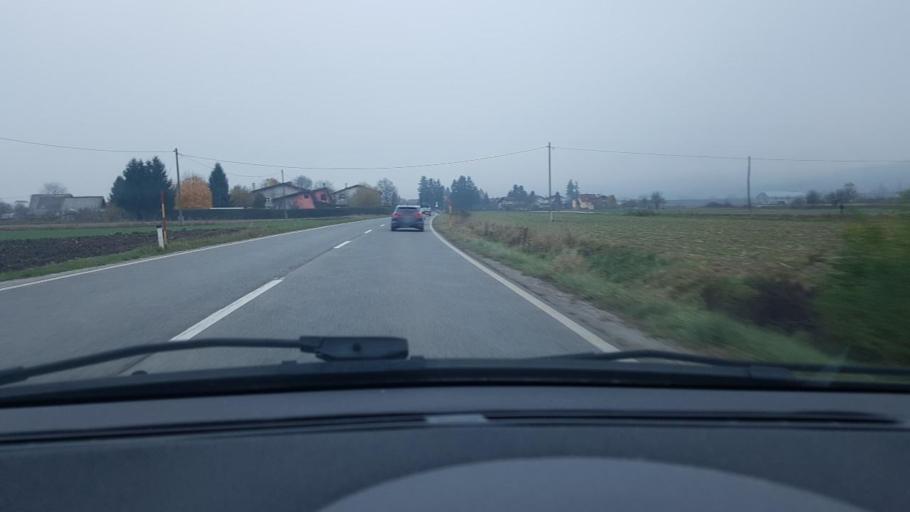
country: SI
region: Zalec
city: Zalec
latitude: 46.2467
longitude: 15.1943
